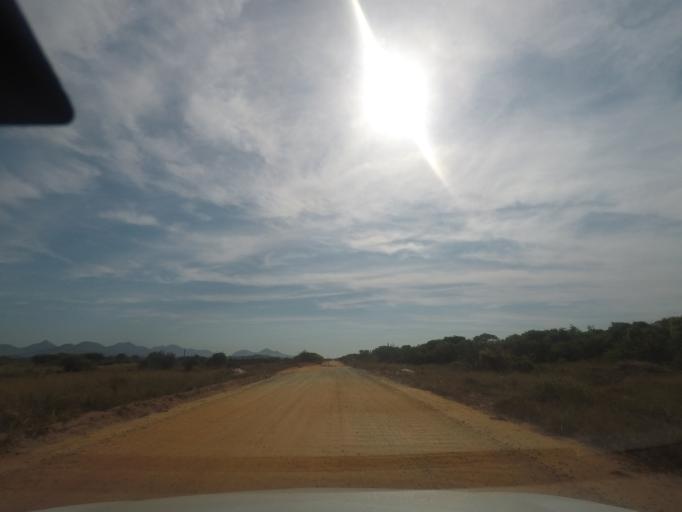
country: BR
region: Rio de Janeiro
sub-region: Marica
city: Marica
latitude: -22.9607
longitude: -42.8559
